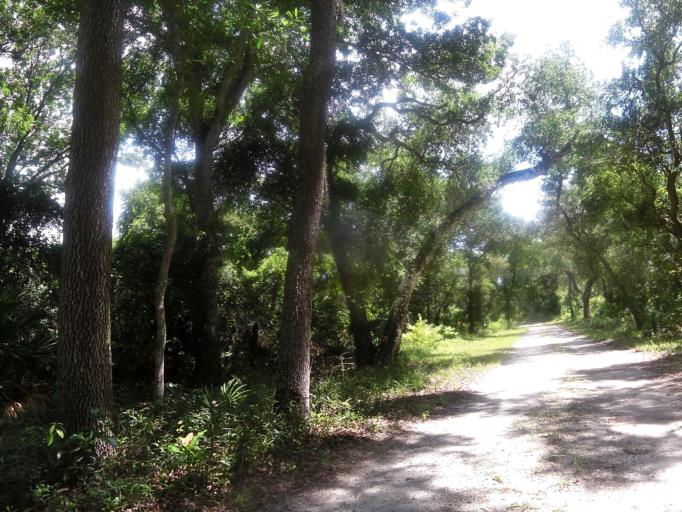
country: US
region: Florida
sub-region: Saint Johns County
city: Villano Beach
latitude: 30.0416
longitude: -81.3376
